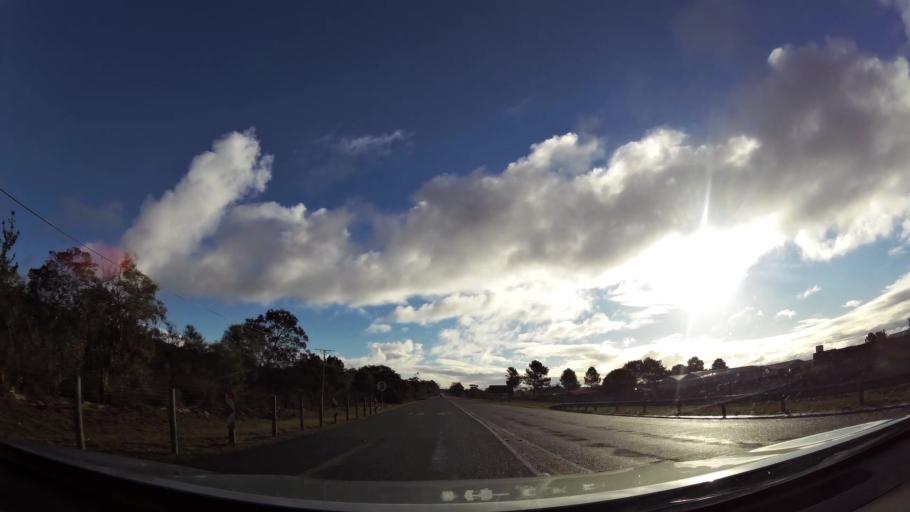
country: ZA
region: Western Cape
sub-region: Eden District Municipality
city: Riversdale
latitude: -34.2127
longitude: 21.5828
